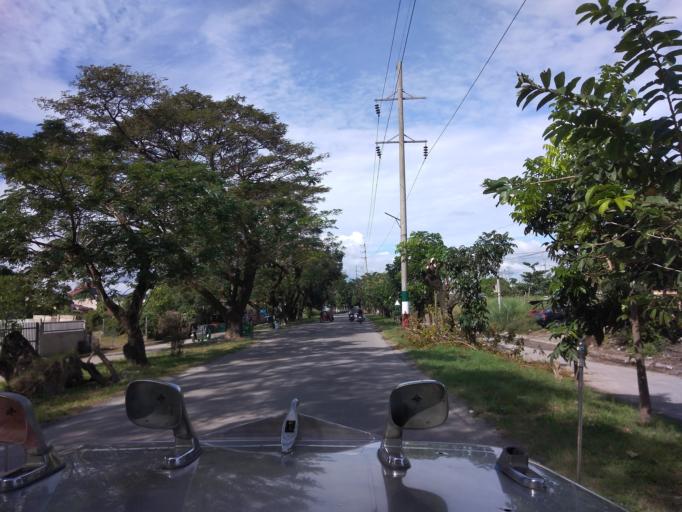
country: PH
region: Central Luzon
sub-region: Province of Pampanga
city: Pandacaqui
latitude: 15.1786
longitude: 120.6523
